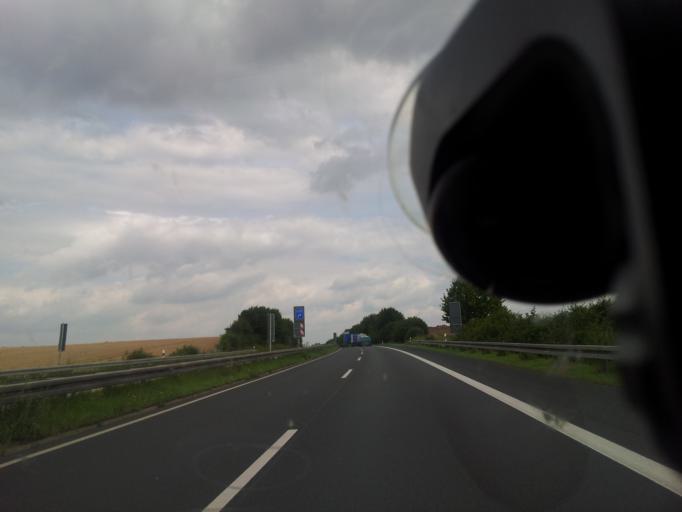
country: DE
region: Lower Saxony
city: Schladen
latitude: 51.9960
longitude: 10.5525
